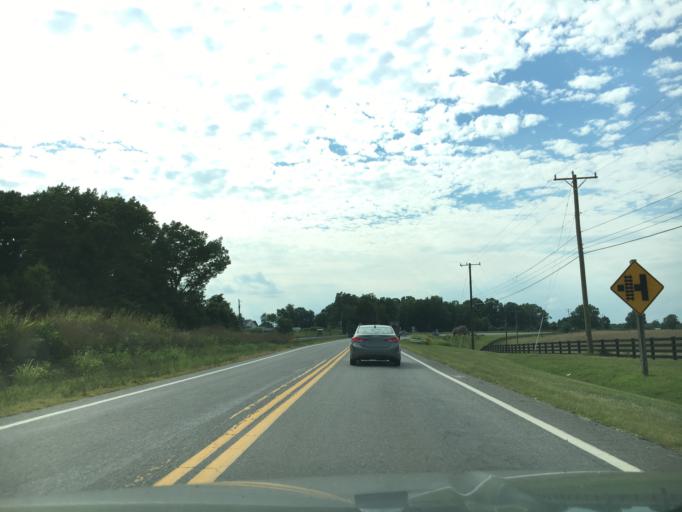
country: US
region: Virginia
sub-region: Campbell County
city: Brookneal
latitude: 37.0745
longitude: -78.9819
